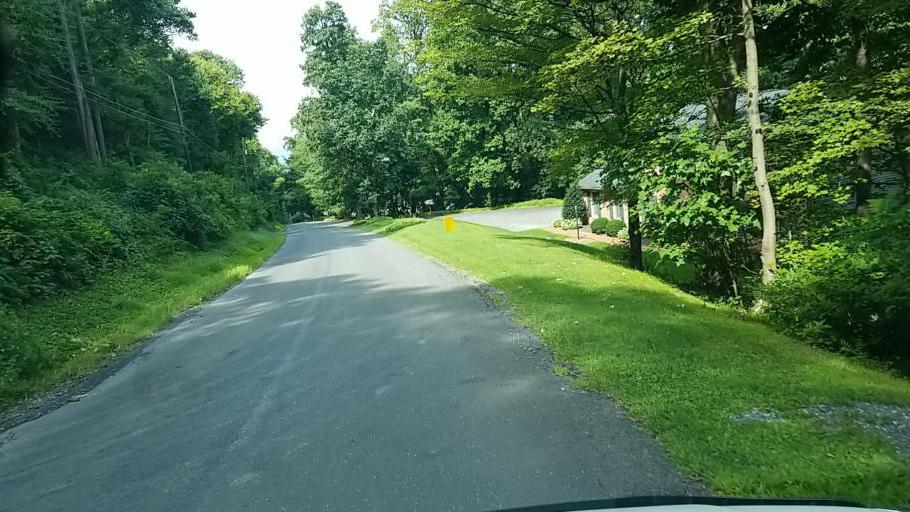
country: US
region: Pennsylvania
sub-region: Dauphin County
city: Millersburg
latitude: 40.5270
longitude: -76.9572
